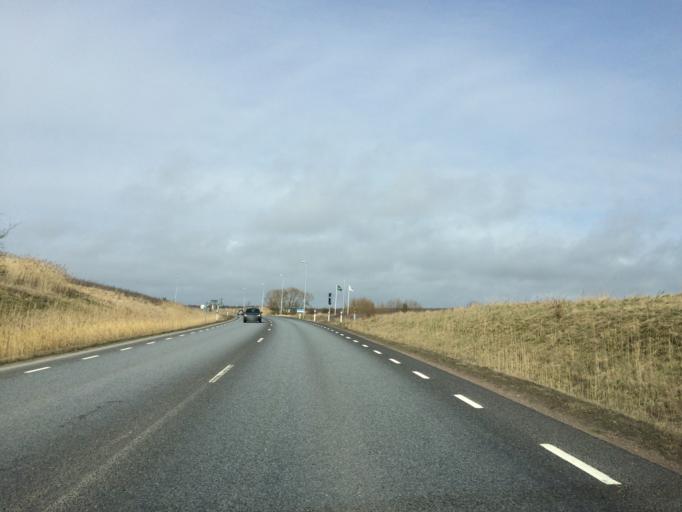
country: SE
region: Halland
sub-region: Halmstads Kommun
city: Troenninge
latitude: 56.6165
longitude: 12.9567
